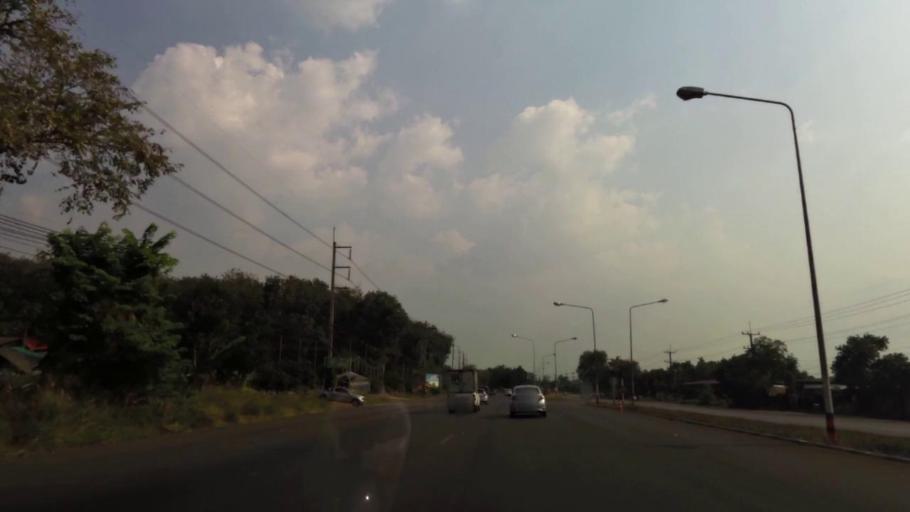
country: TH
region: Rayong
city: Wang Chan
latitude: 12.8881
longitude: 101.5525
